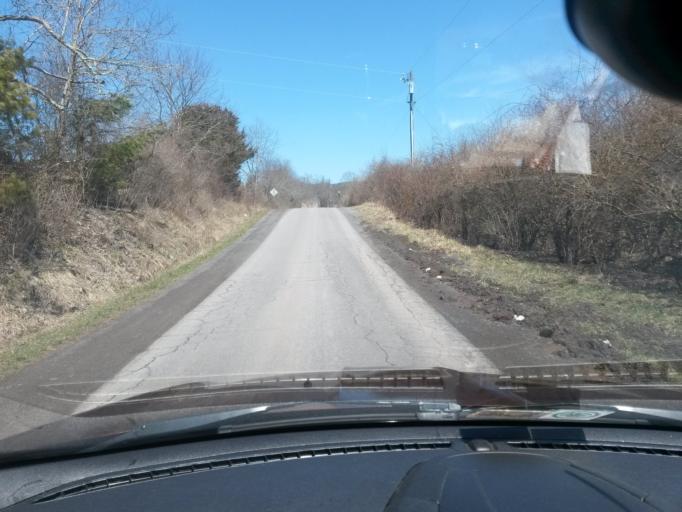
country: US
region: West Virginia
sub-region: Greenbrier County
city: White Sulphur Springs
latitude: 37.6614
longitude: -80.3159
